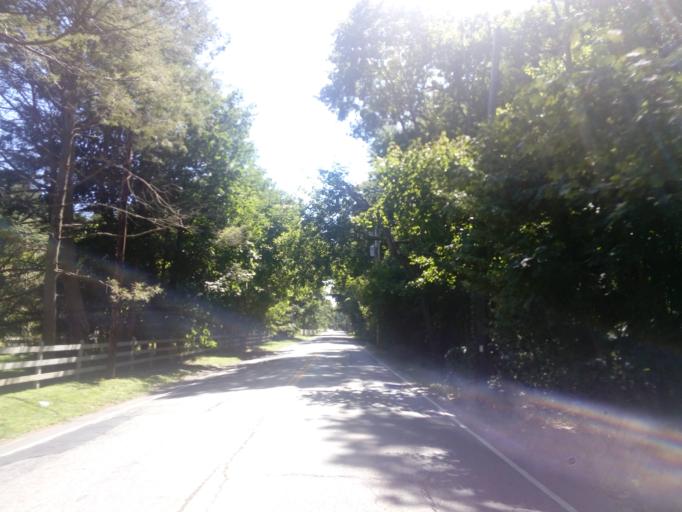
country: US
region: New York
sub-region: Nassau County
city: Upper Brookville
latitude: 40.8461
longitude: -73.5738
